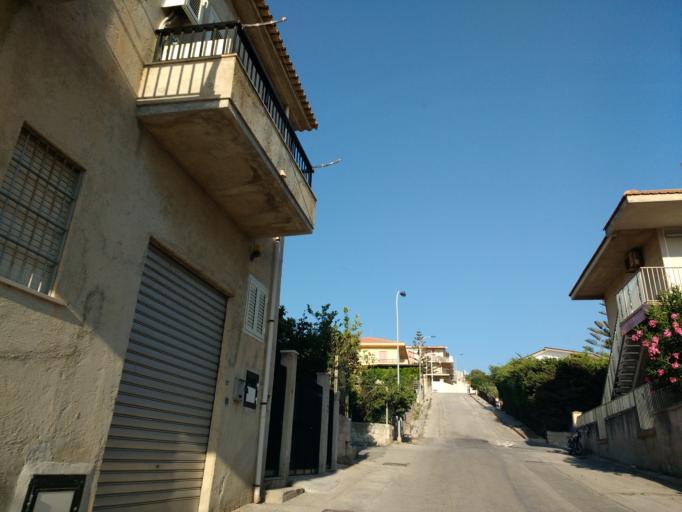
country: IT
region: Sicily
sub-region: Ragusa
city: Cava d'Aliga
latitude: 36.7318
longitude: 14.6888
